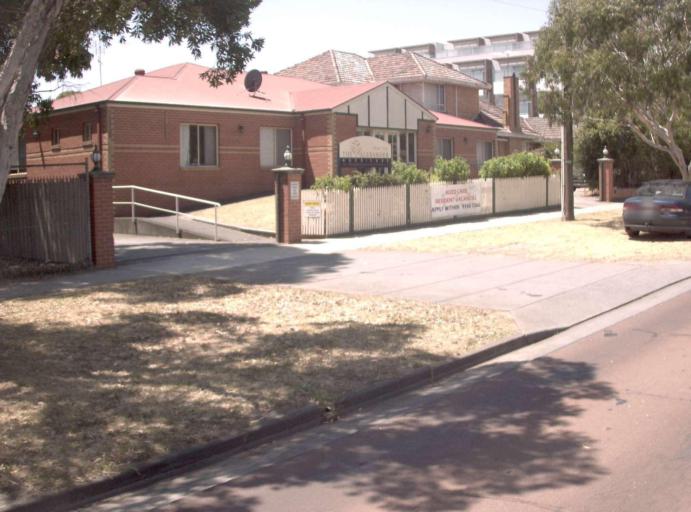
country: AU
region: Victoria
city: Clayton
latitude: -37.9138
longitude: 145.1230
